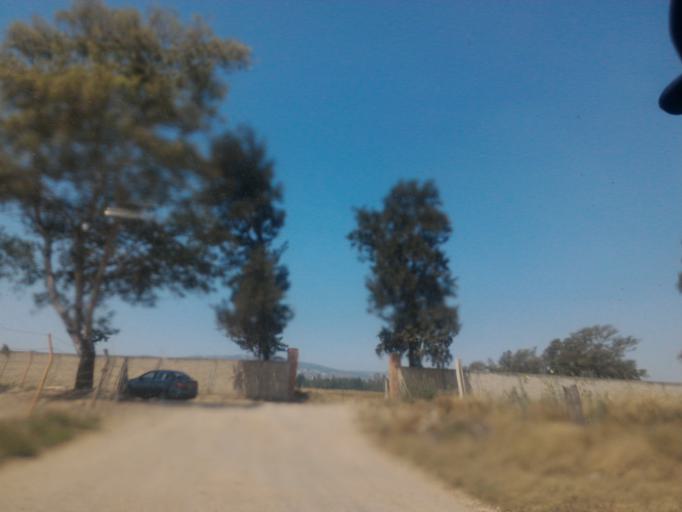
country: MX
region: Jalisco
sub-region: San Pedro Tlaquepaque
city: Paseo del Prado
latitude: 20.5635
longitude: -103.3982
